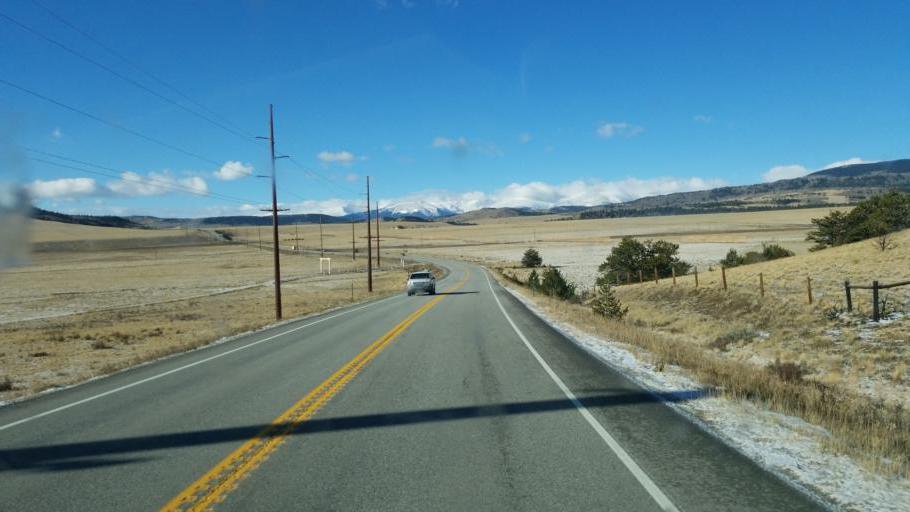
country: US
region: Colorado
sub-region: Park County
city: Fairplay
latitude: 39.2983
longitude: -105.8983
